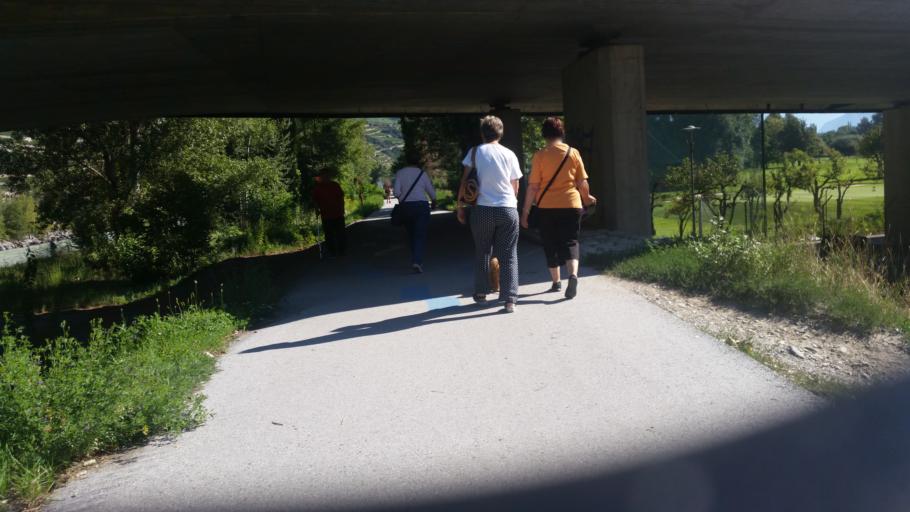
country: CH
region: Valais
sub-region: Sion District
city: Sitten
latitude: 46.2375
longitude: 7.3746
